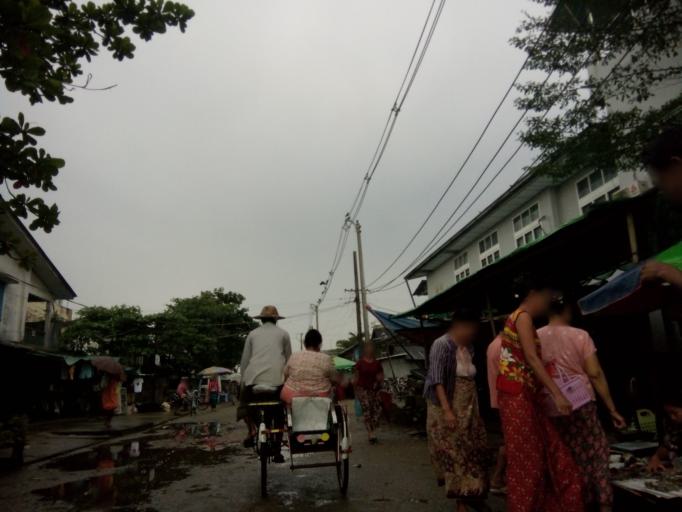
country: MM
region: Yangon
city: Yangon
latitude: 16.9137
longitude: 96.1621
